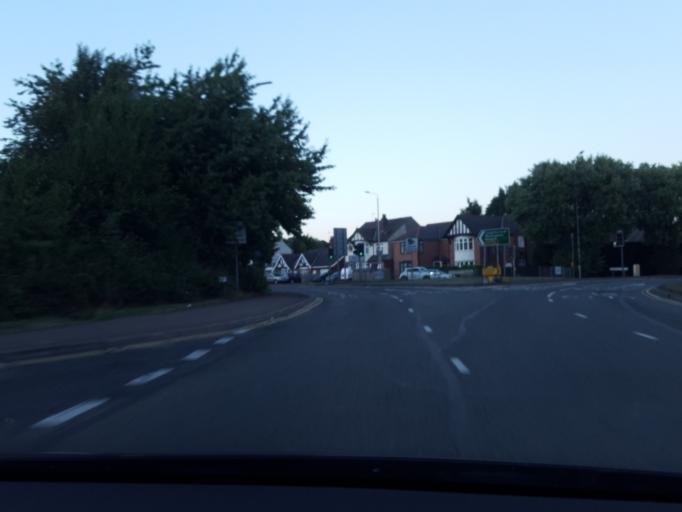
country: GB
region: England
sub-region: City of Leicester
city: Leicester
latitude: 52.6648
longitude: -1.1298
